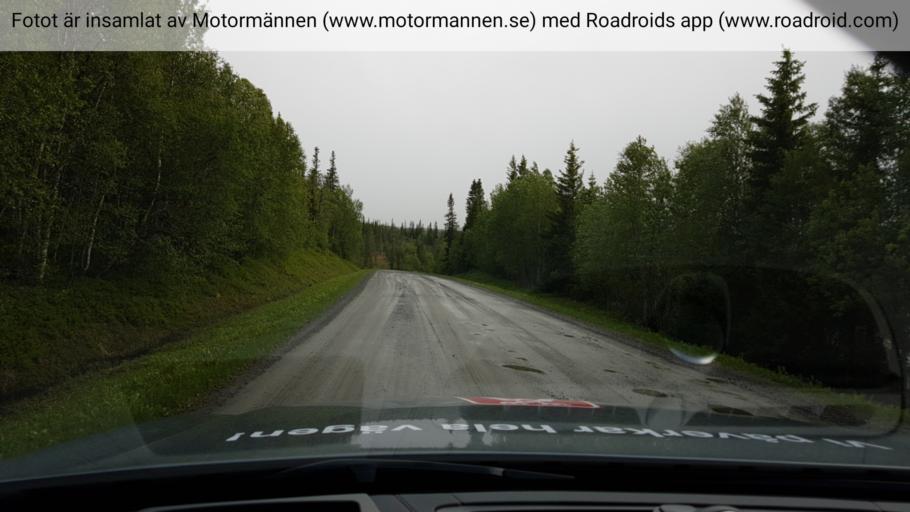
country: NO
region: Nord-Trondelag
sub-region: Snasa
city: Snaase
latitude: 63.7048
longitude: 12.3490
